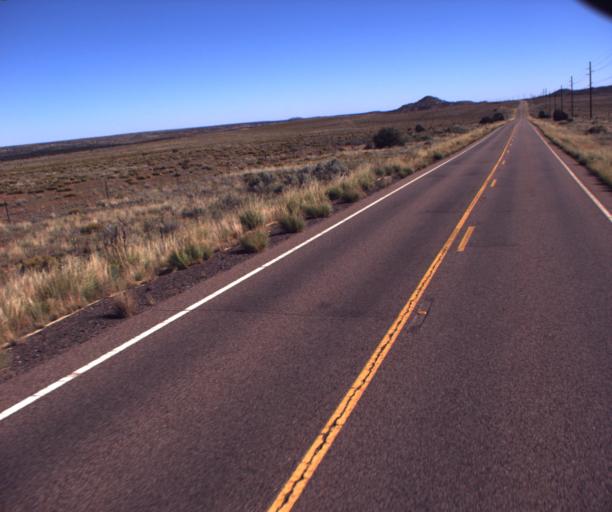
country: US
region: Arizona
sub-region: Navajo County
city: Taylor
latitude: 34.4902
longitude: -110.2298
